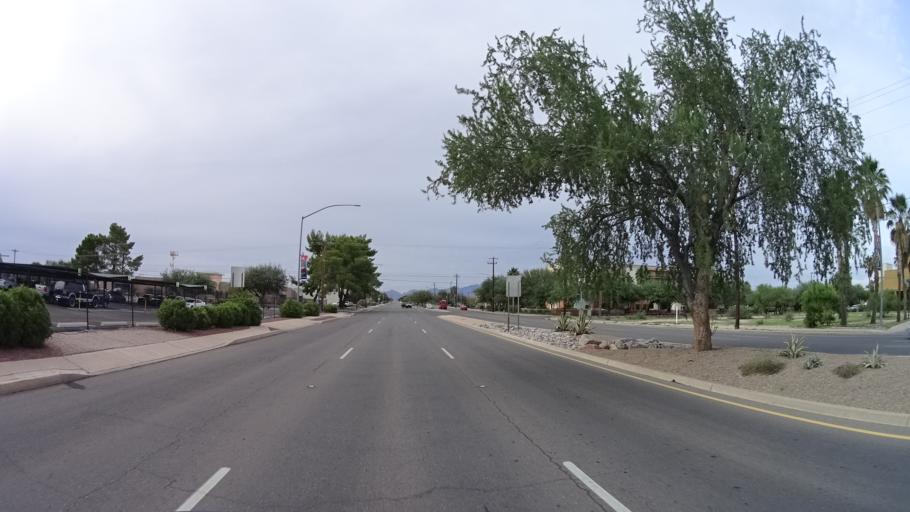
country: US
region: Arizona
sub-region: Pima County
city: Summit
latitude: 32.1262
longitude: -110.9347
